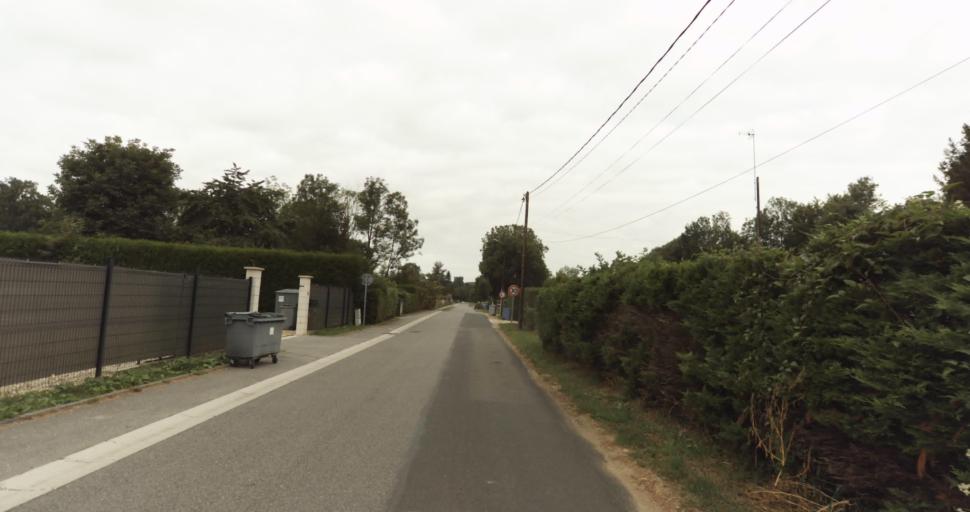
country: FR
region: Haute-Normandie
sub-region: Departement de l'Eure
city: Marcilly-sur-Eure
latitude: 48.8215
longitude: 1.3548
